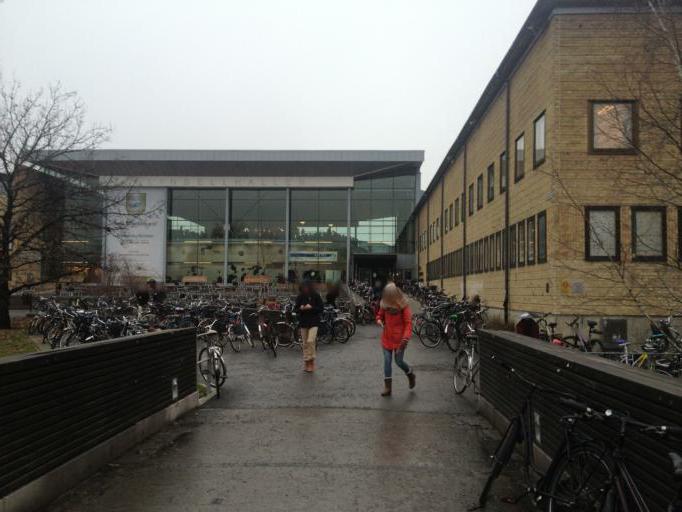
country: SE
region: Vaesterbotten
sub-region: Umea Kommun
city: Umea
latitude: 63.8209
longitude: 20.3059
